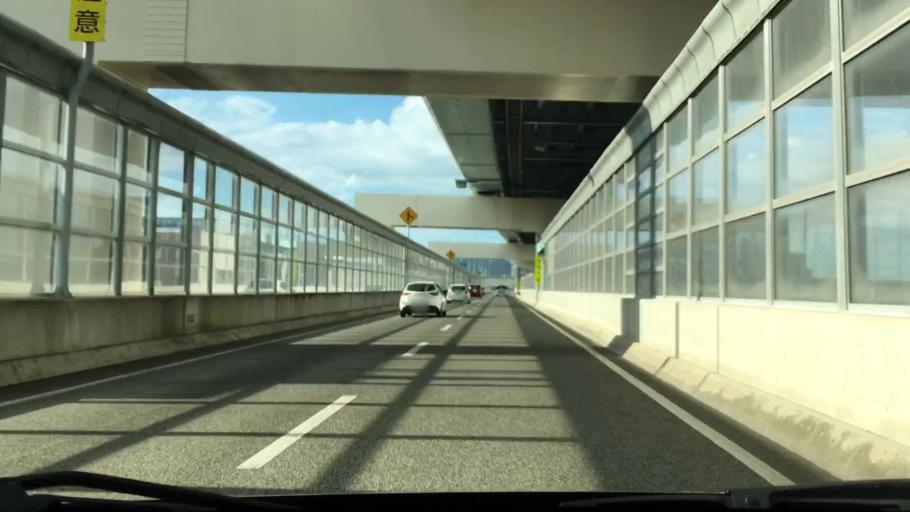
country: JP
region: Fukuoka
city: Fukuoka-shi
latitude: 33.5733
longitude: 130.3164
